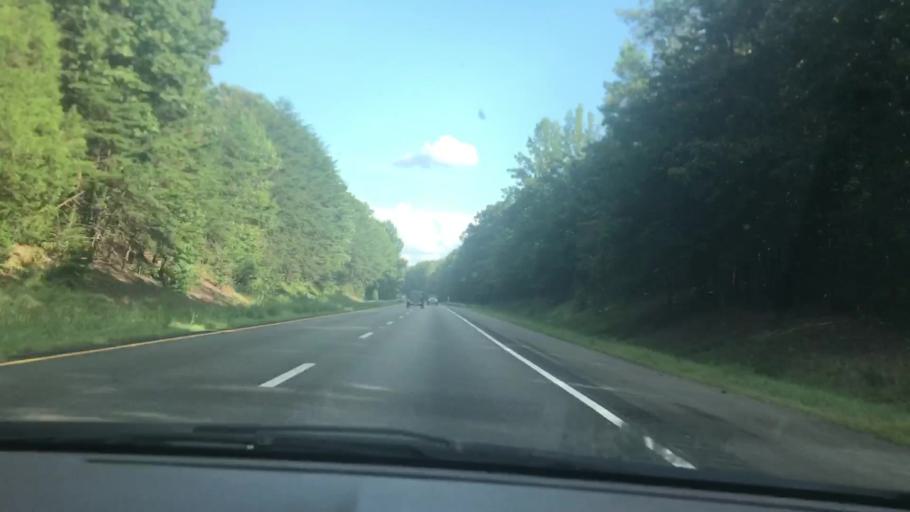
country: US
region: Virginia
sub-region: Goochland County
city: Goochland
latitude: 37.7658
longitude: -77.8705
